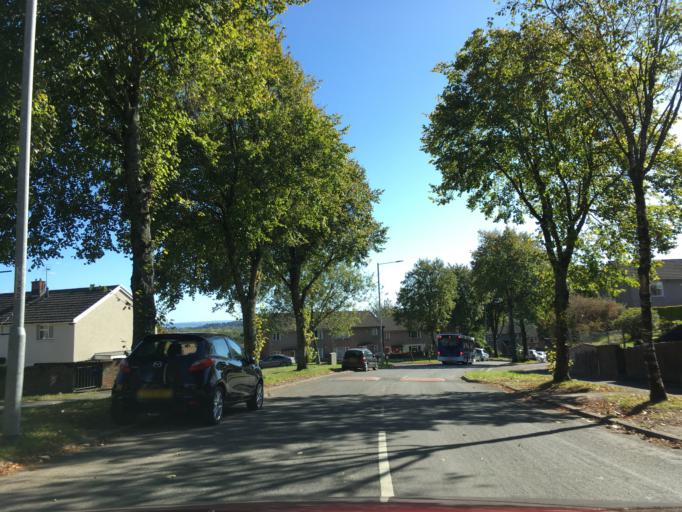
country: GB
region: Wales
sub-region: Torfaen County Borough
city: Cwmbran
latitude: 51.6472
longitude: -3.0316
